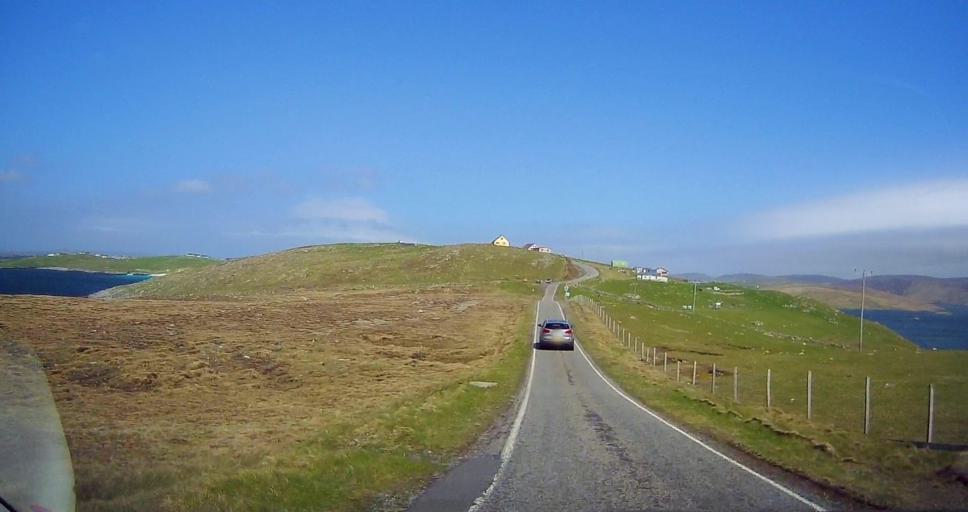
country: GB
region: Scotland
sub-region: Shetland Islands
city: Sandwick
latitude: 60.0923
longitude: -1.3243
